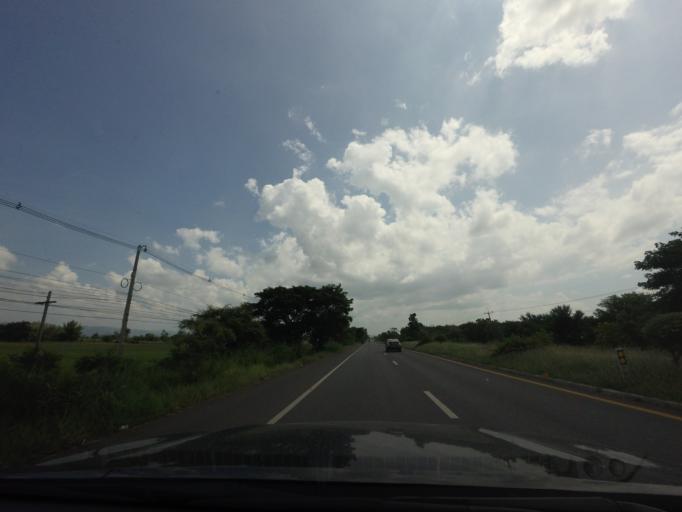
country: TH
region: Phetchabun
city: Phetchabun
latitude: 16.2403
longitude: 101.0772
